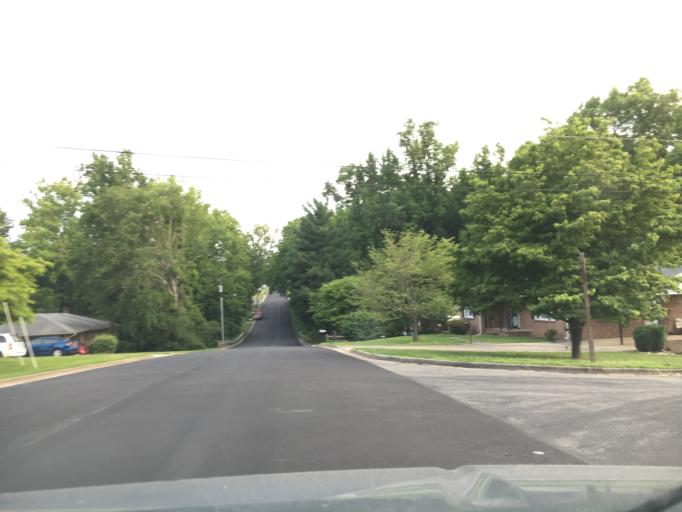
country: US
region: Virginia
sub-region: Halifax County
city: South Boston
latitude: 36.7029
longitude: -78.8860
